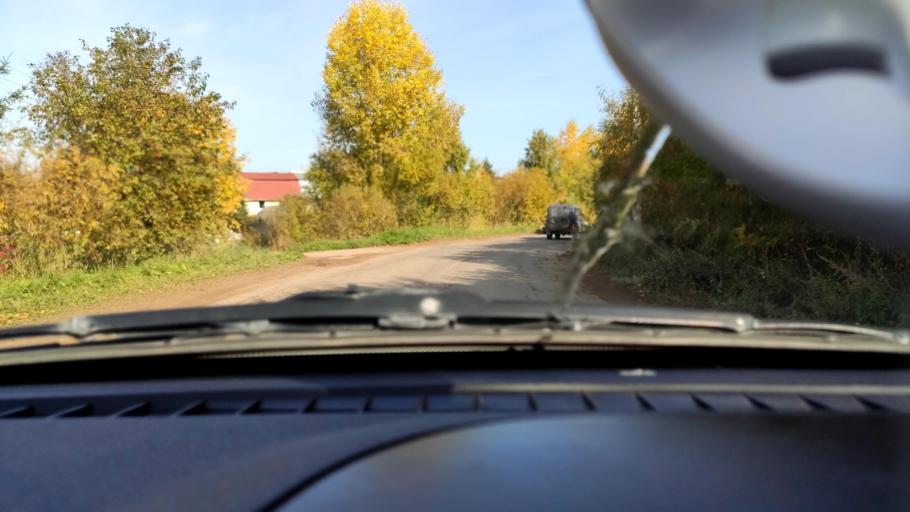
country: RU
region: Perm
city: Overyata
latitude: 58.0763
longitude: 55.8874
